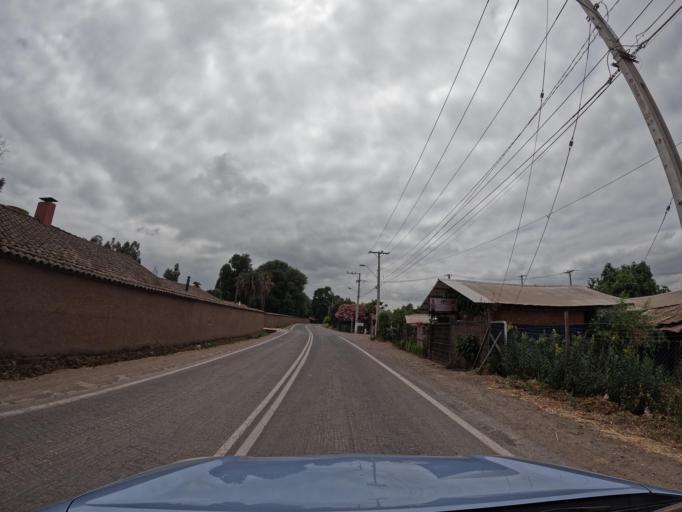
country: CL
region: Maule
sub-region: Provincia de Curico
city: Teno
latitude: -34.7588
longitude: -71.2061
